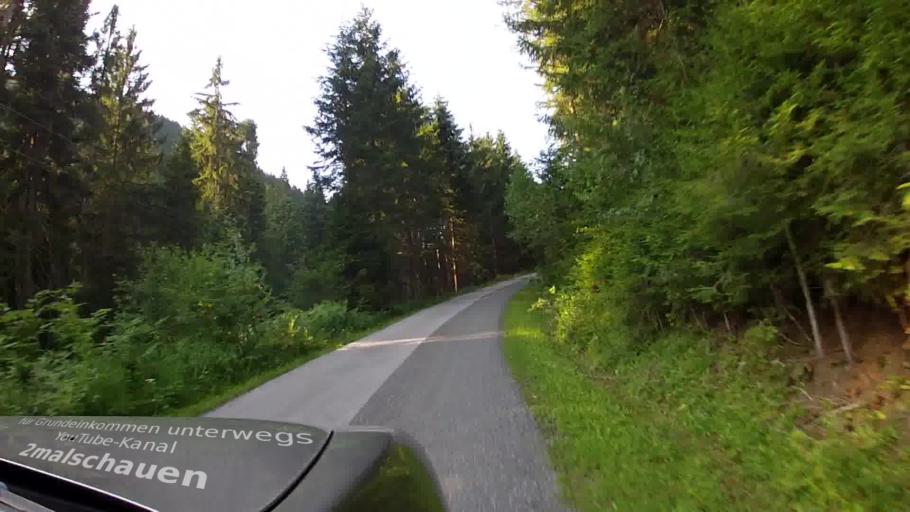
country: AT
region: Salzburg
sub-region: Politischer Bezirk Sankt Johann im Pongau
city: Eben im Pongau
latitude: 47.4347
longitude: 13.3807
